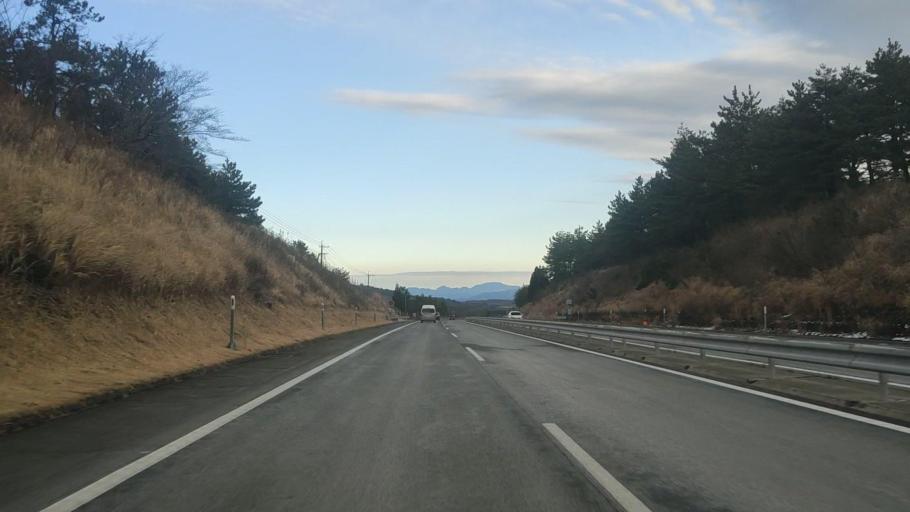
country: JP
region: Oita
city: Beppu
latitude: 33.3234
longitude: 131.4148
